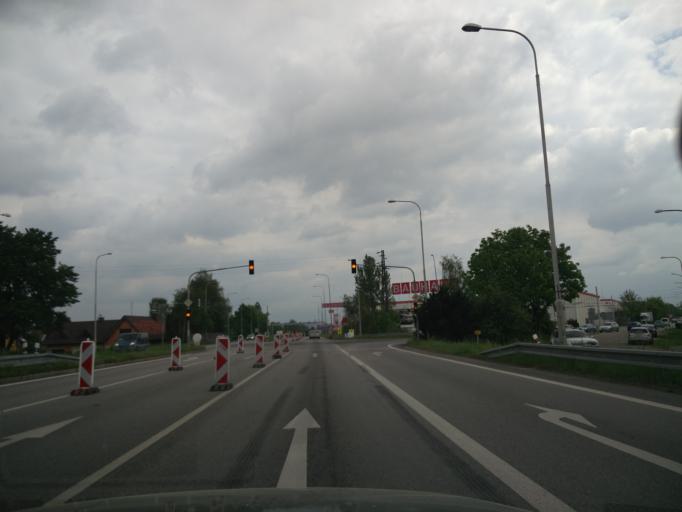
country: CZ
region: Jihocesky
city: Hrdejovice
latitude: 49.0087
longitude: 14.4458
